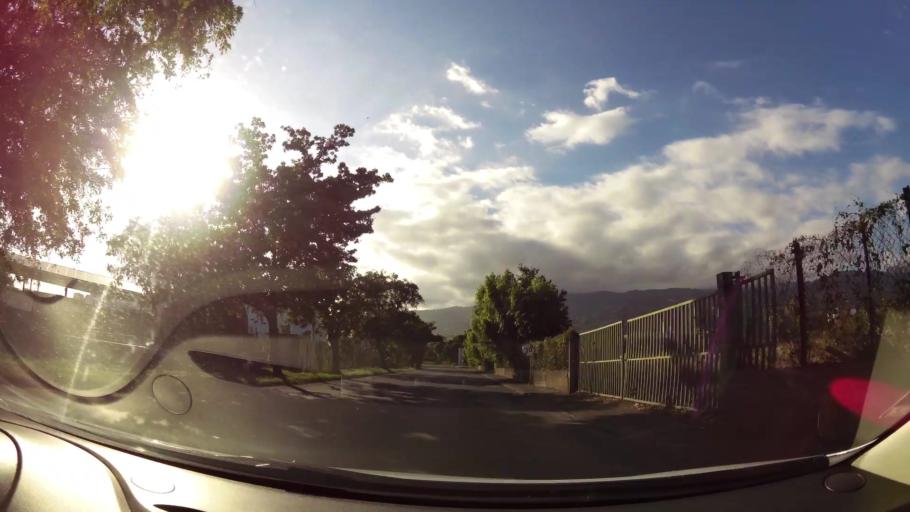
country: RE
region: Reunion
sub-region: Reunion
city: Saint-Louis
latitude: -21.2764
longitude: 55.3731
